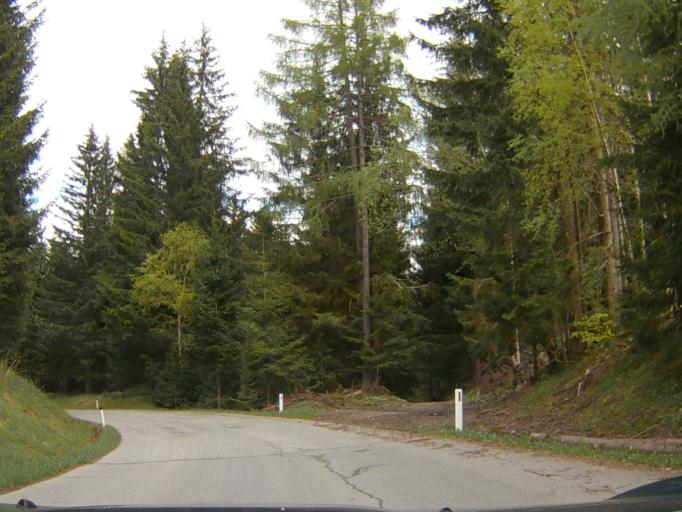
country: AT
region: Carinthia
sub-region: Politischer Bezirk Villach Land
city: Stockenboi
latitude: 46.7395
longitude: 13.5461
